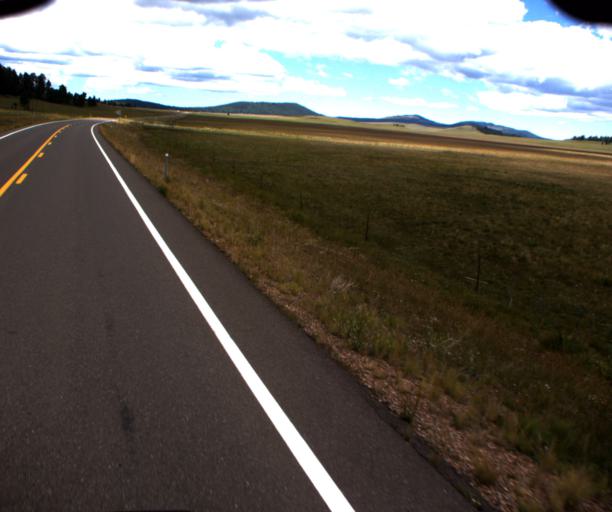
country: US
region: Arizona
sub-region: Apache County
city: Eagar
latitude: 33.9925
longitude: -109.5167
